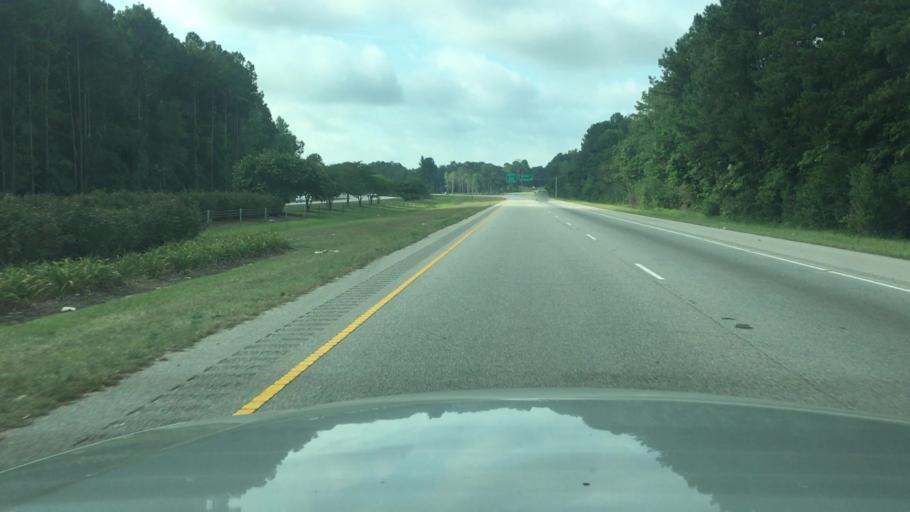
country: US
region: North Carolina
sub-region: Cumberland County
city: Fayetteville
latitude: 34.9851
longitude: -78.8608
